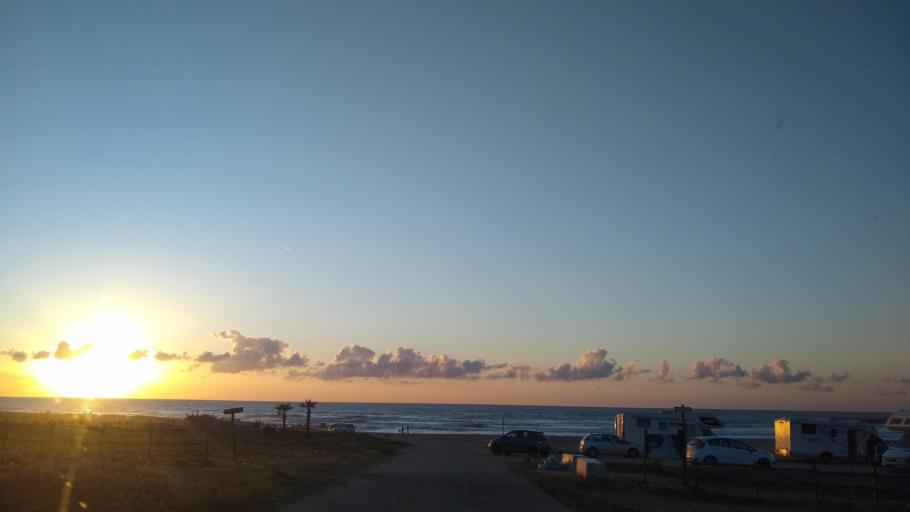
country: IT
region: Sicily
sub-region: Trapani
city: Castelluzzo
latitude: 38.1235
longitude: 12.7295
